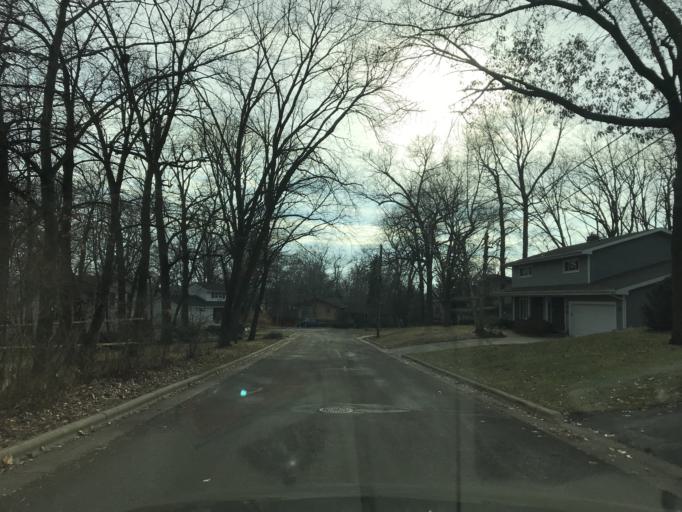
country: US
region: Wisconsin
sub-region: Dane County
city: Monona
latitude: 43.0595
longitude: -89.3494
